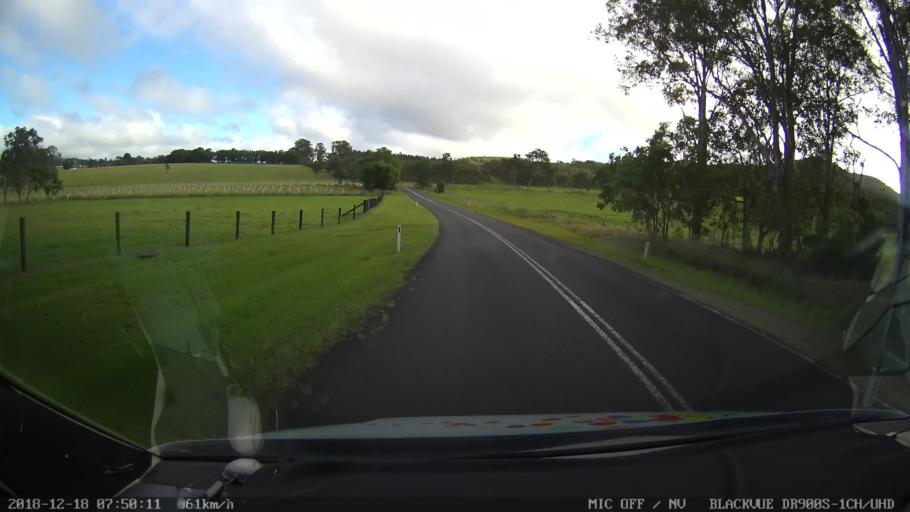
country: AU
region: New South Wales
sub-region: Kyogle
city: Kyogle
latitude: -28.4478
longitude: 152.5737
